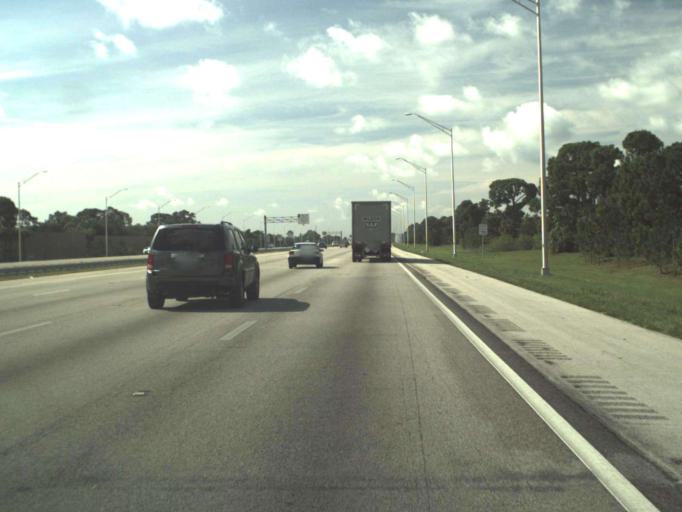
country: US
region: Florida
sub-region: Palm Beach County
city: Limestone Creek
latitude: 26.9092
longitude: -80.1418
